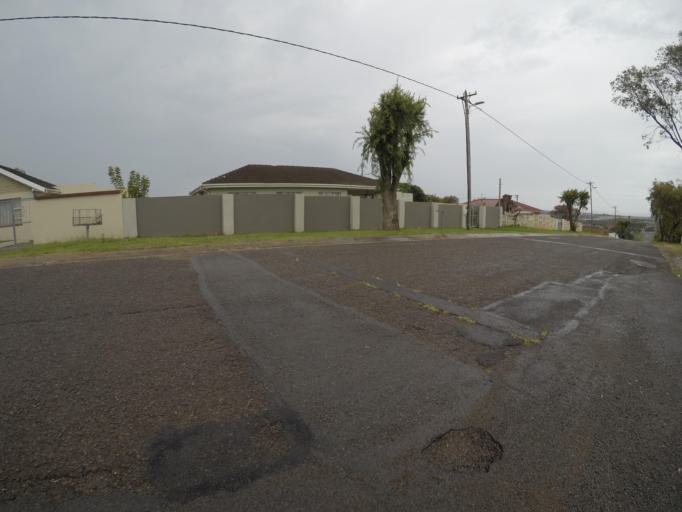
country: ZA
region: Eastern Cape
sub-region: Buffalo City Metropolitan Municipality
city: East London
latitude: -32.9864
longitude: 27.8607
